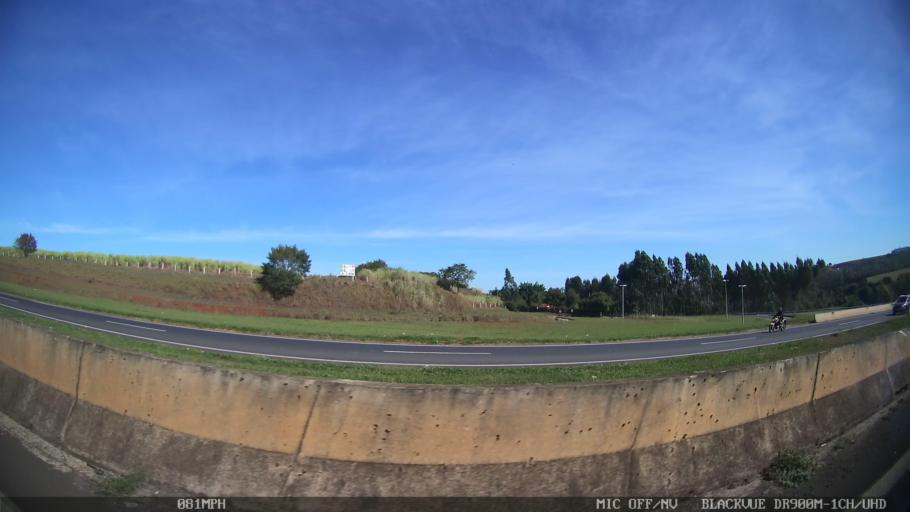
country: BR
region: Sao Paulo
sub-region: Leme
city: Leme
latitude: -22.1027
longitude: -47.4146
